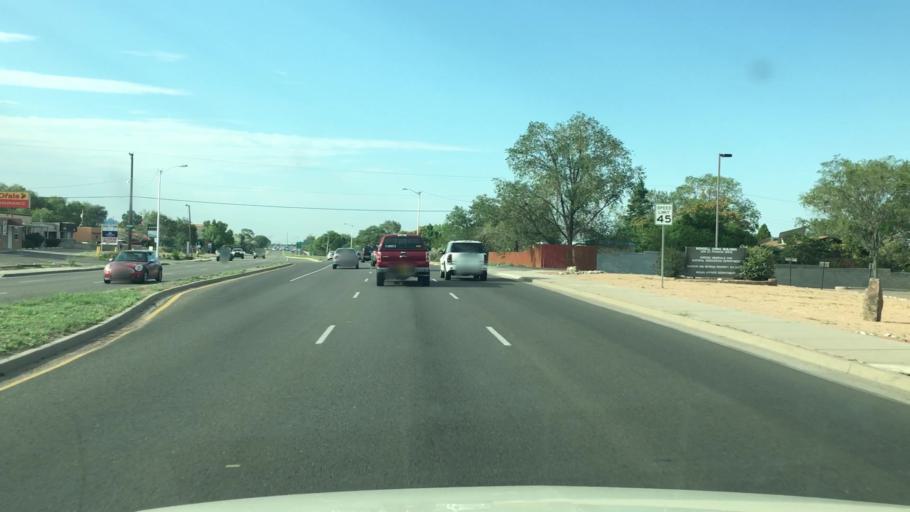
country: US
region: New Mexico
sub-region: Santa Fe County
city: Santa Fe
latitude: 35.6693
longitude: -105.9560
